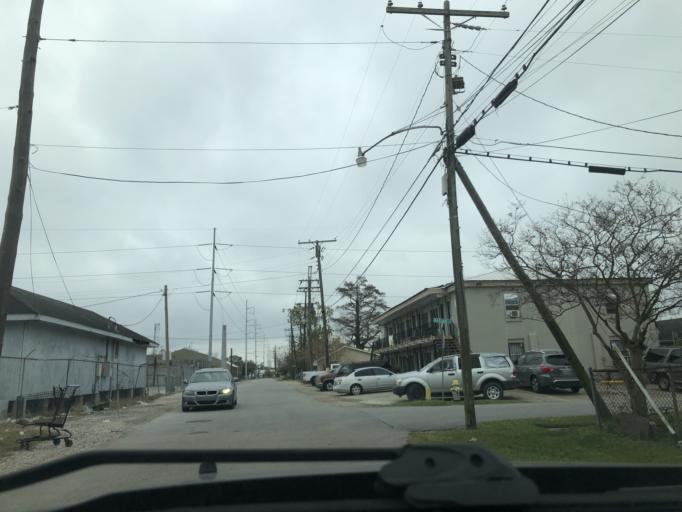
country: US
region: Louisiana
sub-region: Jefferson Parish
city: Metairie Terrace
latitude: 29.9727
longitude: -90.1631
